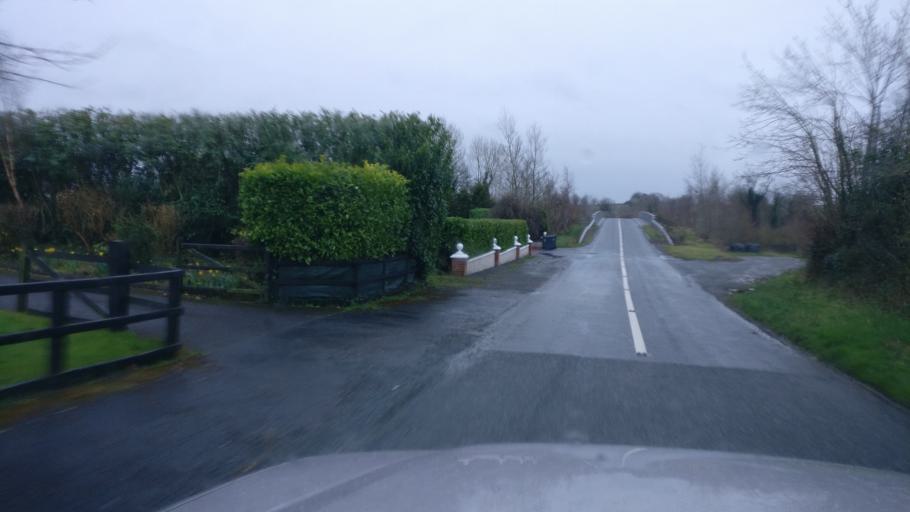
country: IE
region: Connaught
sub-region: County Galway
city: Ballinasloe
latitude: 53.3085
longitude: -8.2795
